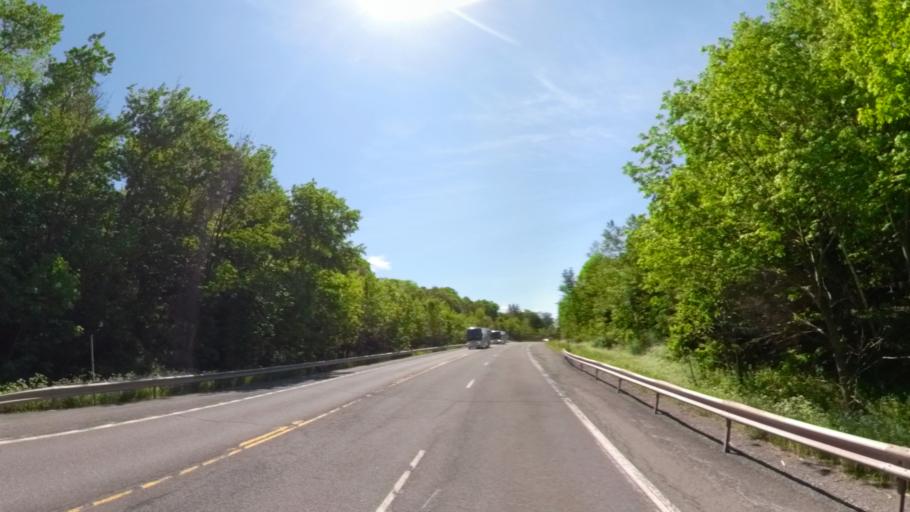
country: US
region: New York
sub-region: Delaware County
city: Stamford
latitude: 42.1490
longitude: -74.4972
